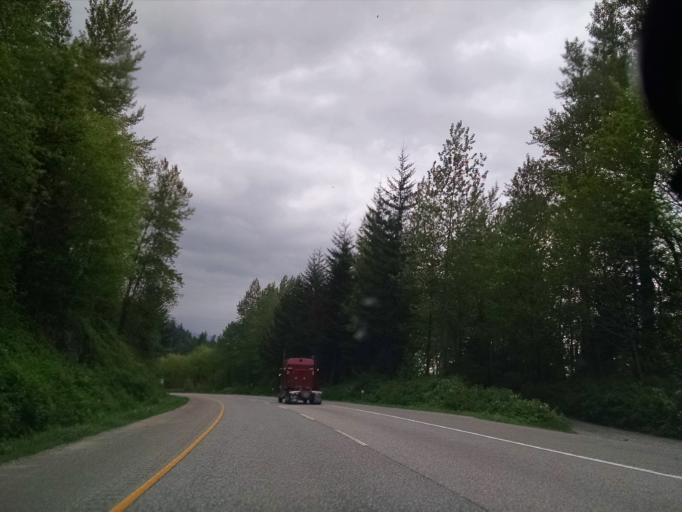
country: CA
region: British Columbia
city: Agassiz
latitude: 49.2721
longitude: -121.6753
